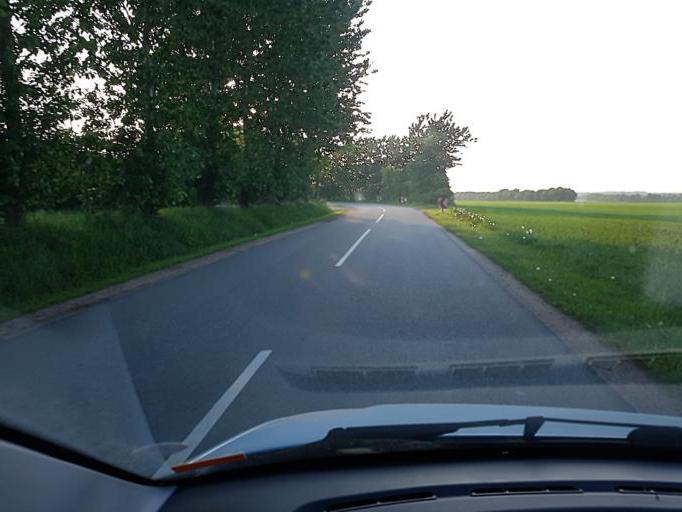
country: DK
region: South Denmark
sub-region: Esbjerg Kommune
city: Tjaereborg
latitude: 55.5485
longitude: 8.5561
